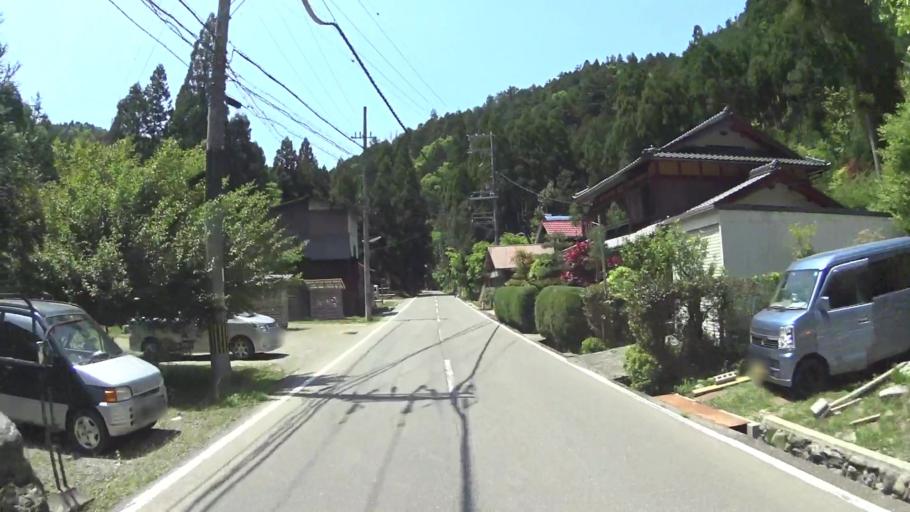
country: JP
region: Kyoto
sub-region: Kyoto-shi
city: Kamigyo-ku
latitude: 35.1971
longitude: 135.7079
